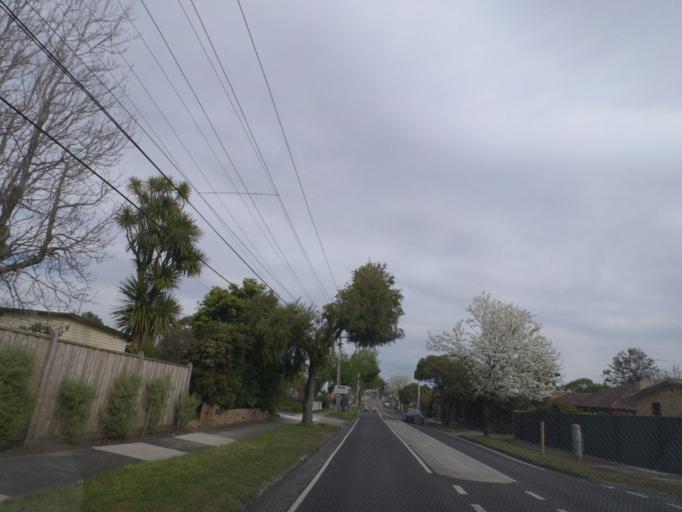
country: AU
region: Victoria
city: Forest Hill
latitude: -37.8287
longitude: 145.1868
